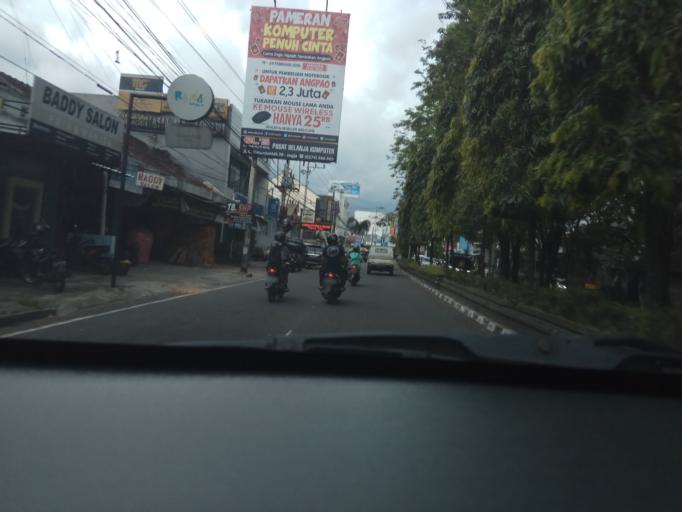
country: ID
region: Daerah Istimewa Yogyakarta
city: Yogyakarta
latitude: -7.7663
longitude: 110.3919
